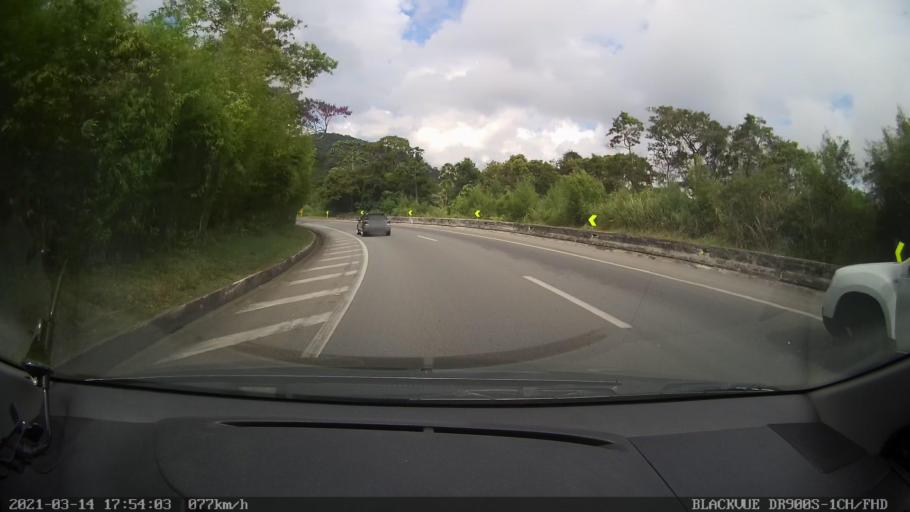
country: BR
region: Rio de Janeiro
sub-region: Petropolis
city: Petropolis
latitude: -22.4851
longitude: -43.2301
